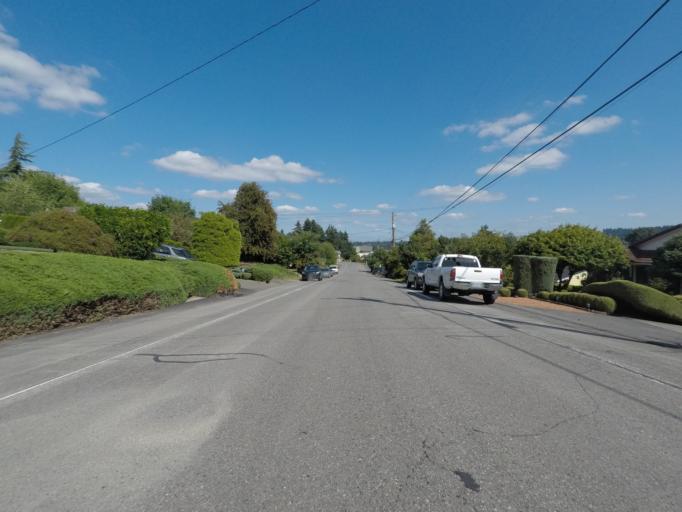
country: US
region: Washington
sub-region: King County
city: Lake Forest Park
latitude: 47.7588
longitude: -122.2662
